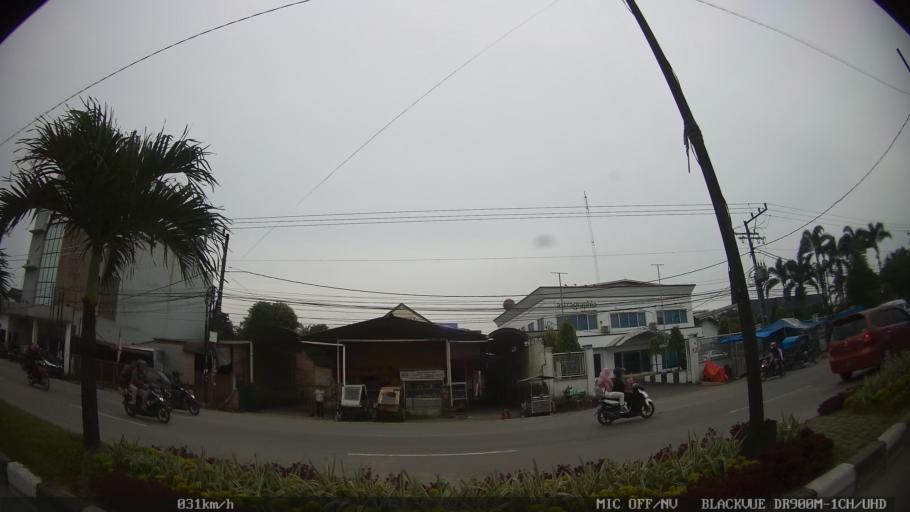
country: ID
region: North Sumatra
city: Deli Tua
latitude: 3.5390
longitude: 98.7016
